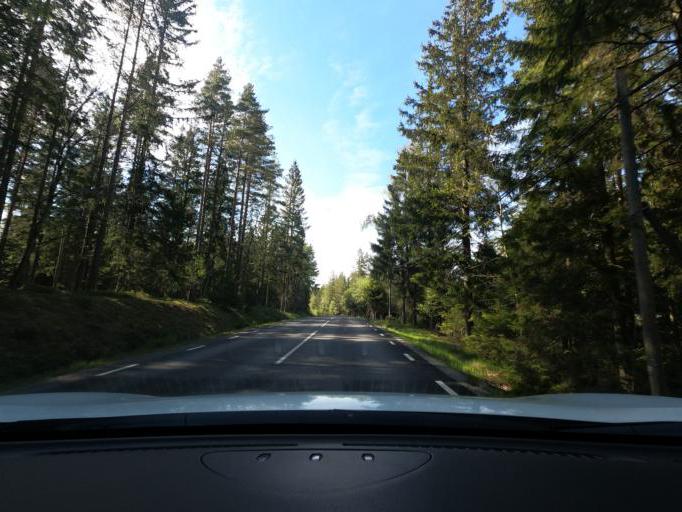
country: SE
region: Vaestra Goetaland
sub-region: Harryda Kommun
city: Landvetter
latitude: 57.6285
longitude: 12.2749
